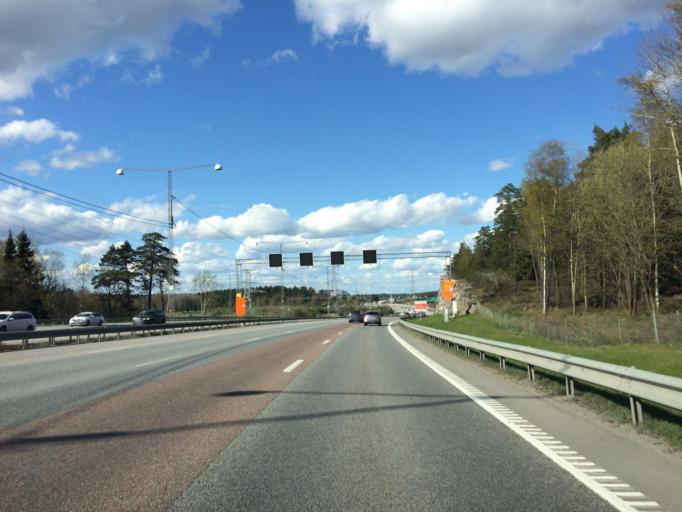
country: SE
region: Stockholm
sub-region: Sollentuna Kommun
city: Sollentuna
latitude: 59.4306
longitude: 17.9218
